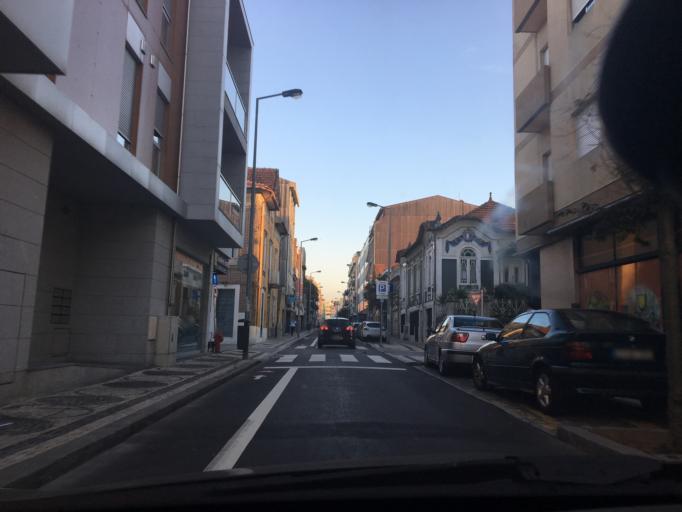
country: PT
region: Porto
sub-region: Matosinhos
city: Matosinhos
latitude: 41.1852
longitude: -8.6907
